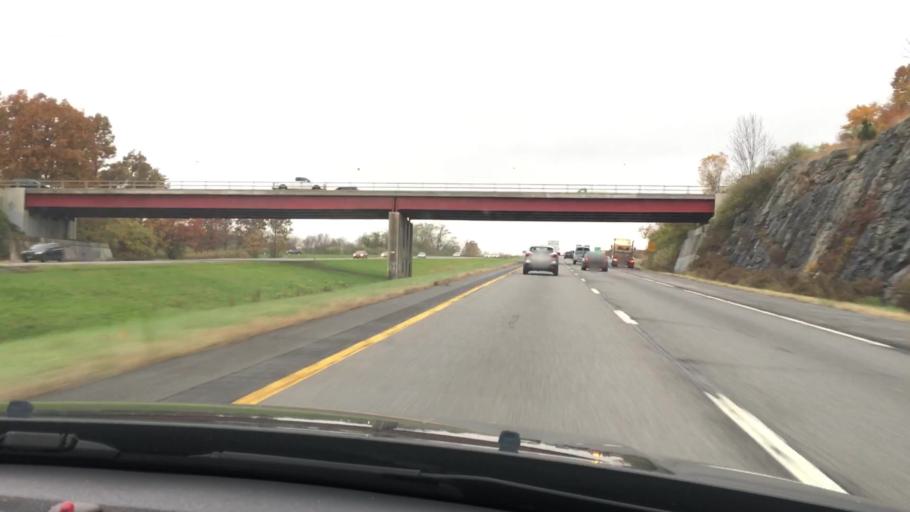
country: US
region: New York
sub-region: Putnam County
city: Brewster Hill
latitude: 41.4243
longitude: -73.6259
